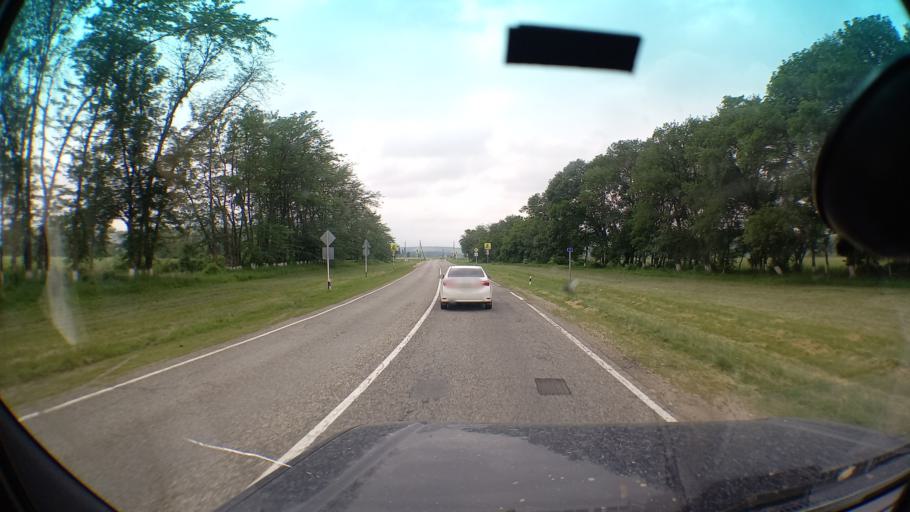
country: RU
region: Krasnodarskiy
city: Mostovskoy
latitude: 44.4503
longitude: 40.7698
